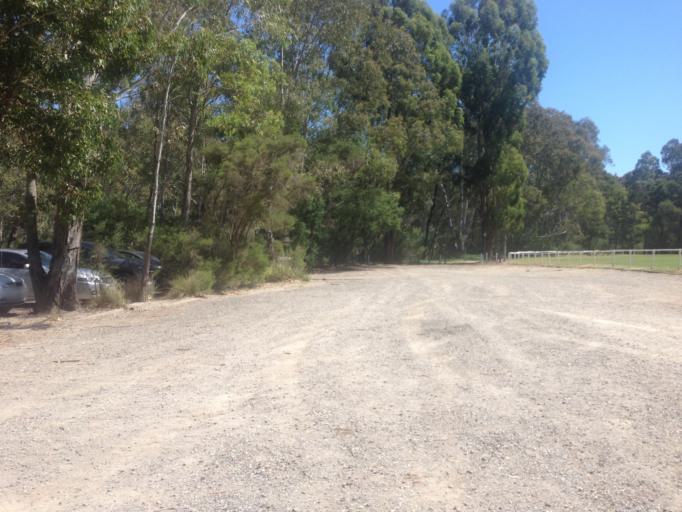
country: AU
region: Victoria
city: Ivanhoe East
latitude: -37.7783
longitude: 145.0495
